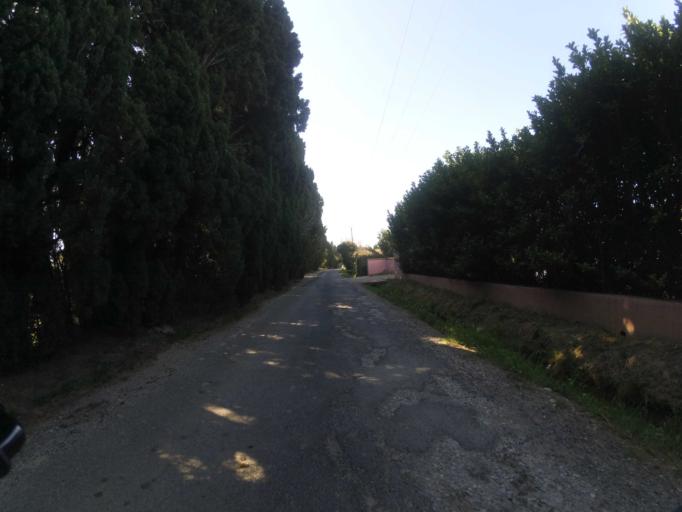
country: FR
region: Languedoc-Roussillon
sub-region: Departement des Pyrenees-Orientales
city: Pezilla-la-Riviere
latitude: 42.7020
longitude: 2.7731
